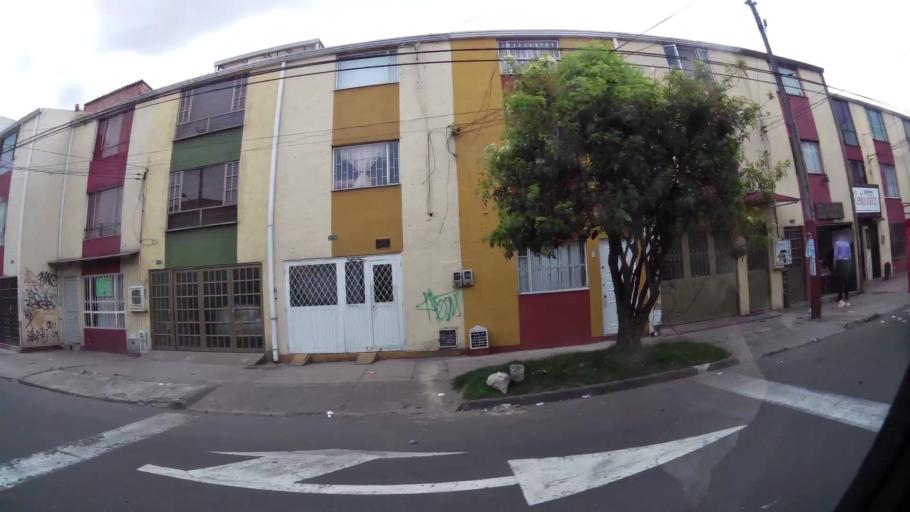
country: CO
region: Cundinamarca
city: Funza
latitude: 4.7166
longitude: -74.1257
